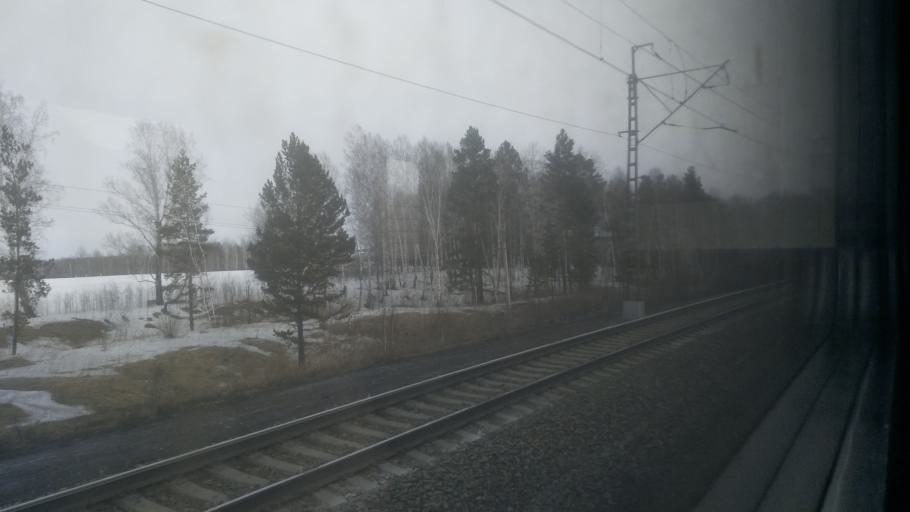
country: RU
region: Novosibirsk
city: Stantsionno-Oyashinskiy
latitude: 55.5106
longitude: 83.9346
